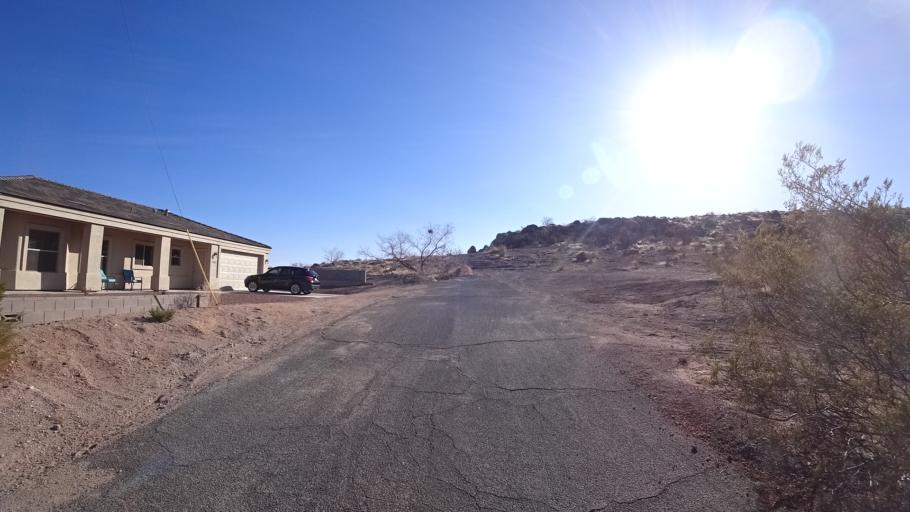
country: US
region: Arizona
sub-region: Mohave County
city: Kingman
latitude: 35.2103
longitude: -114.0092
